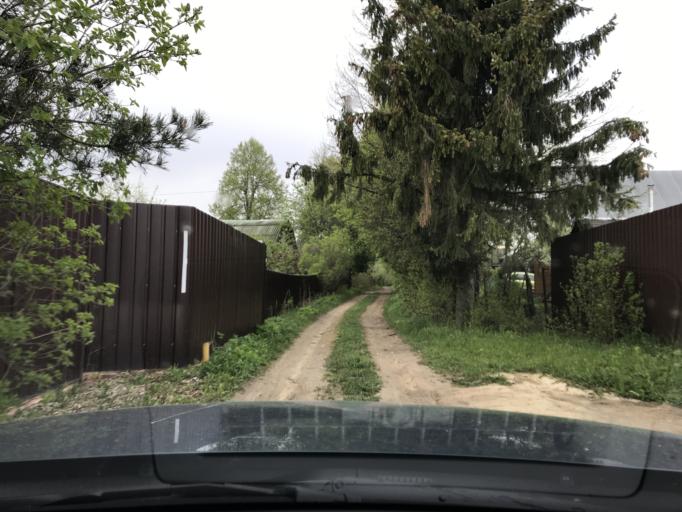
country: RU
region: Kaluga
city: Borovsk
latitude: 55.3191
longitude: 36.3495
